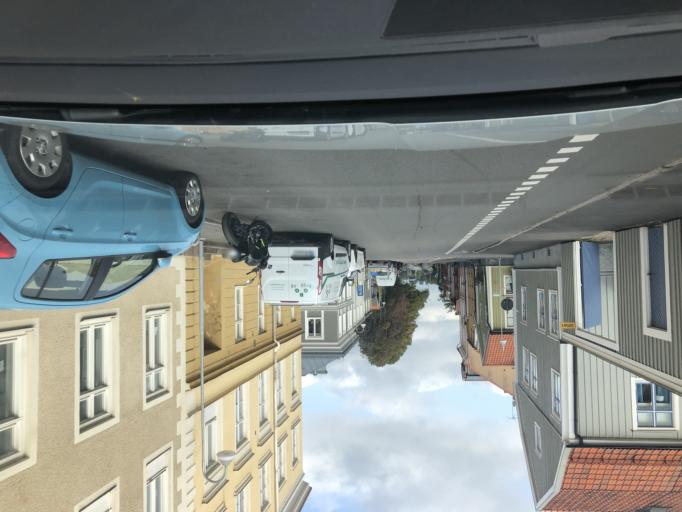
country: SE
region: Kalmar
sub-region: Kalmar Kommun
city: Kalmar
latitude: 56.6650
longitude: 16.3703
